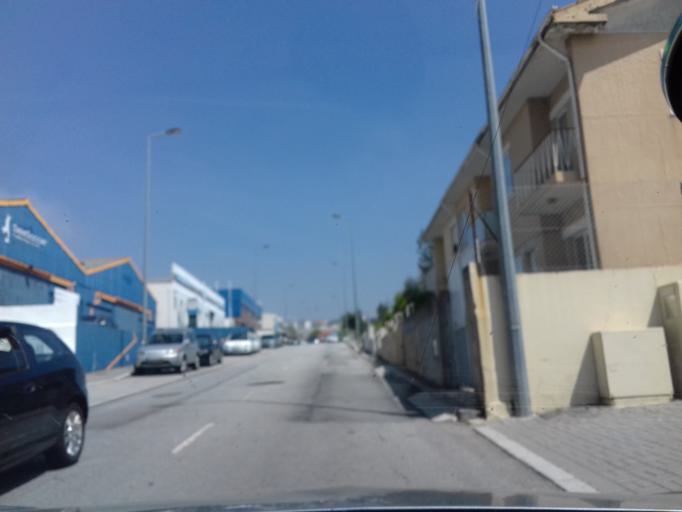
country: PT
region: Porto
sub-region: Vila Nova de Gaia
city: Canelas
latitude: 41.0917
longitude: -8.6034
